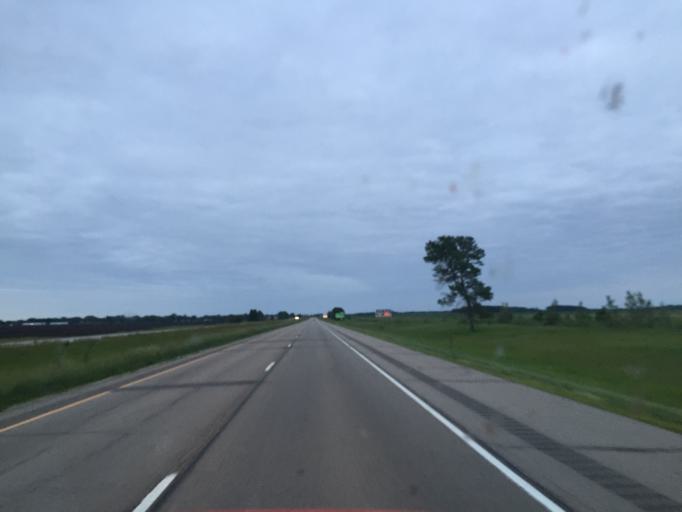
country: US
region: Minnesota
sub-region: Mower County
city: Austin
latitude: 43.6596
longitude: -93.0493
